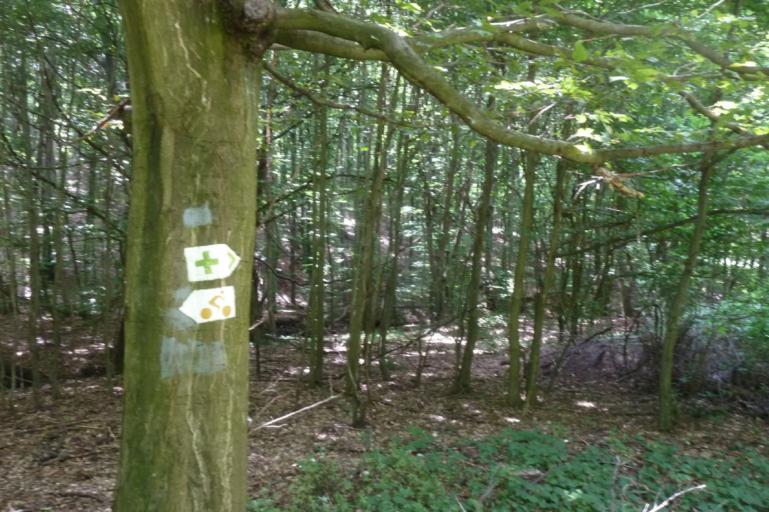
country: HU
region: Pest
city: Szob
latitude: 47.9083
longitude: 18.8891
